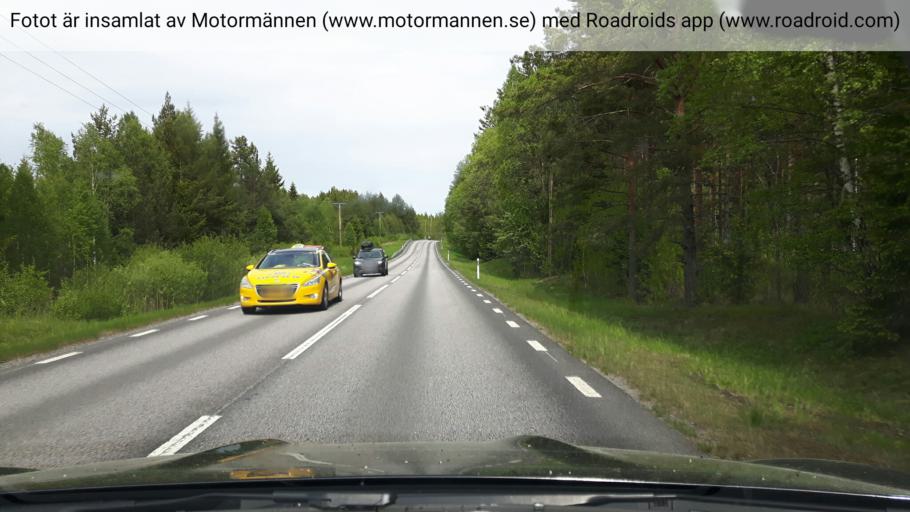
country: SE
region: Stockholm
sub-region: Norrtalje Kommun
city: Norrtalje
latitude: 59.5789
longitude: 18.6511
